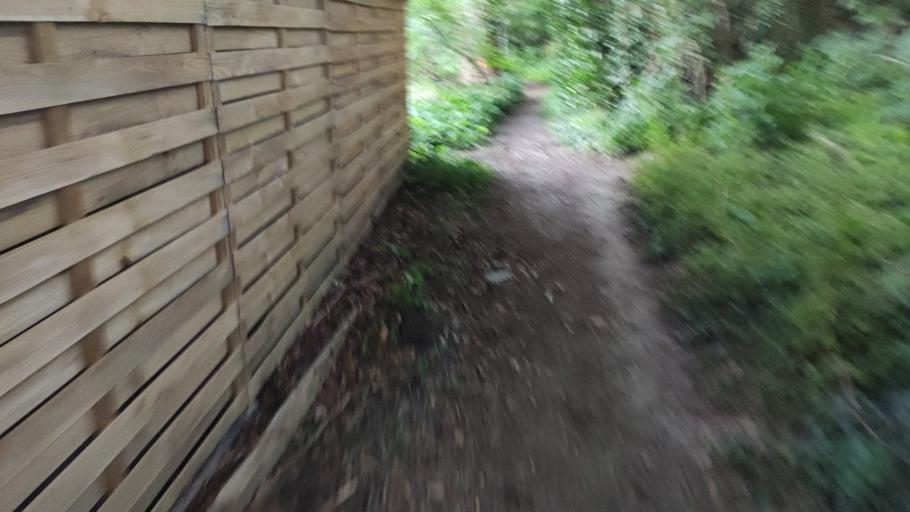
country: BE
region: Flanders
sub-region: Provincie Vlaams-Brabant
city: Hoegaarden
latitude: 50.7618
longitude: 4.8868
